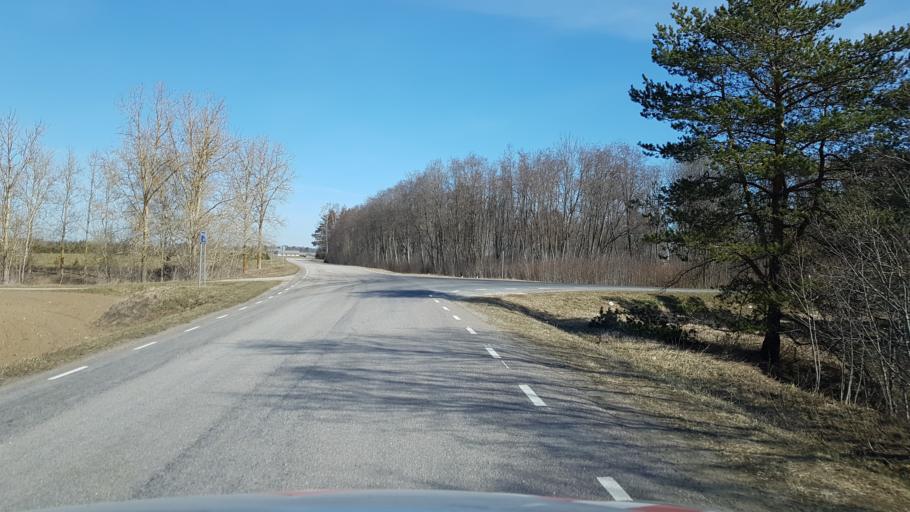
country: EE
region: Laeaene-Virumaa
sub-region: Vinni vald
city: Vinni
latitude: 59.2424
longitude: 26.3514
